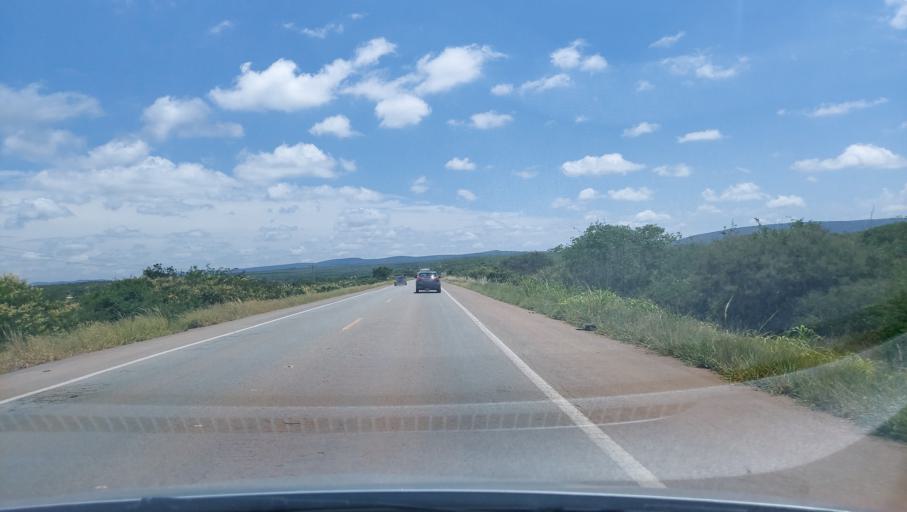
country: BR
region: Bahia
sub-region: Seabra
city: Seabra
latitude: -12.3982
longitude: -41.9387
